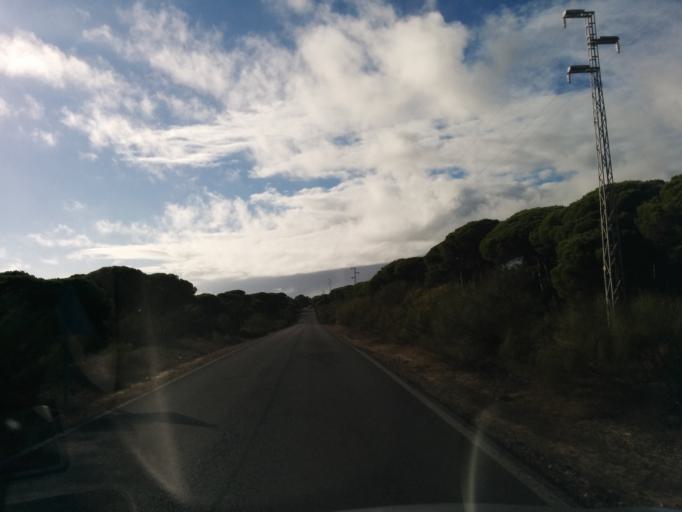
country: ES
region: Andalusia
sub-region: Provincia de Cadiz
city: Vejer de la Frontera
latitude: 36.1927
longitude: -5.9872
